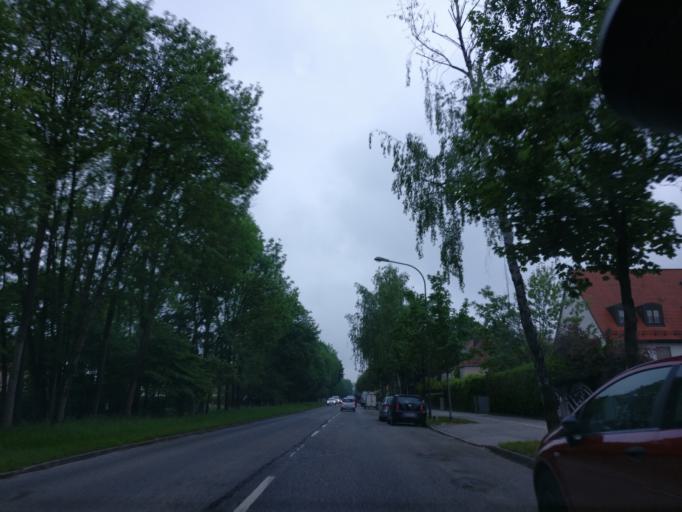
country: DE
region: Bavaria
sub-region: Upper Bavaria
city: Dachau
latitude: 48.2566
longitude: 11.4615
